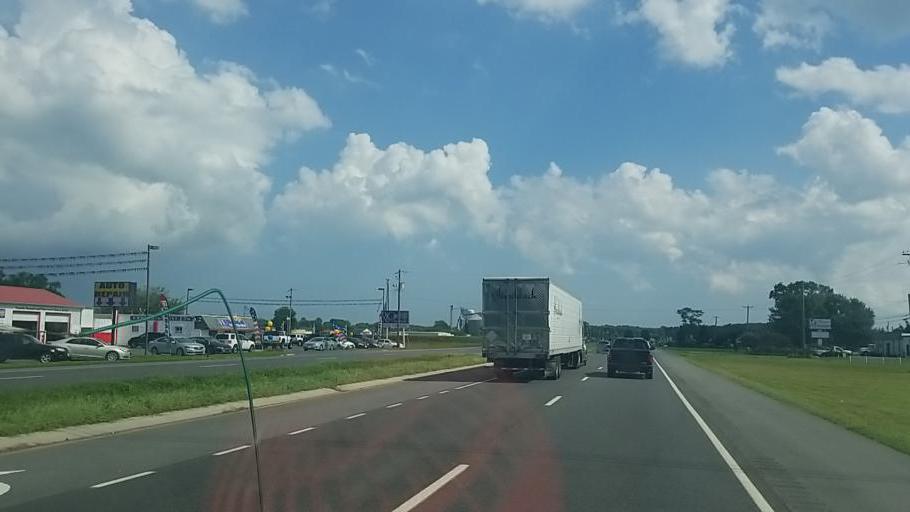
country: US
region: Delaware
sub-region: Sussex County
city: Selbyville
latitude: 38.5245
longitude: -75.2451
